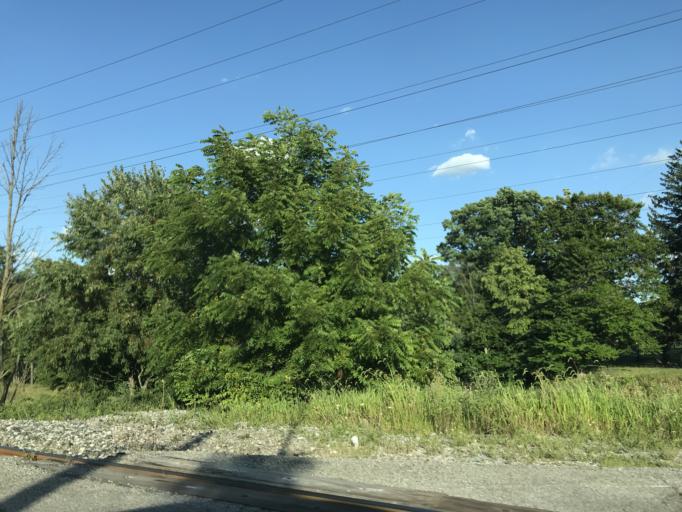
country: US
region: Ohio
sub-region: Cuyahoga County
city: Middleburg Heights
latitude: 41.3634
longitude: -81.8252
